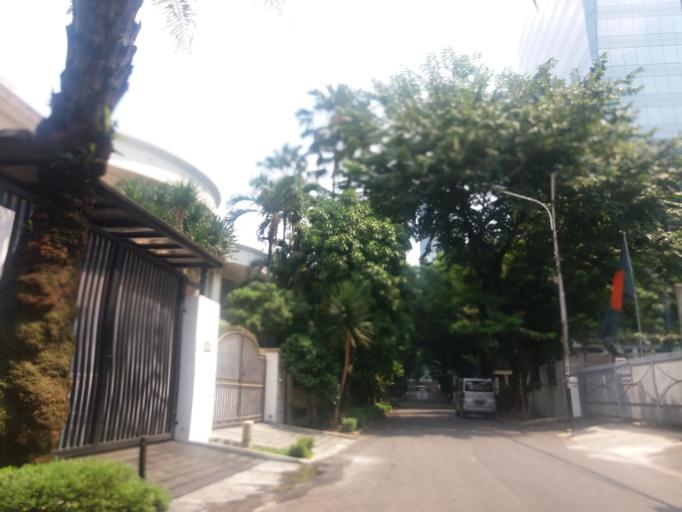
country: ID
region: Jakarta Raya
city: Jakarta
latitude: -6.2259
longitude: 106.8289
